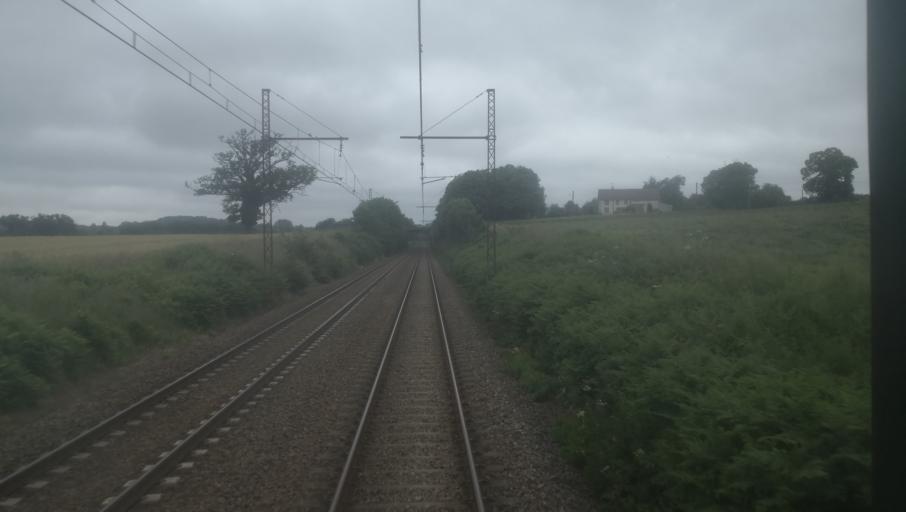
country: FR
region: Limousin
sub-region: Departement de la Creuse
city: La Souterraine
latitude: 46.2051
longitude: 1.4775
